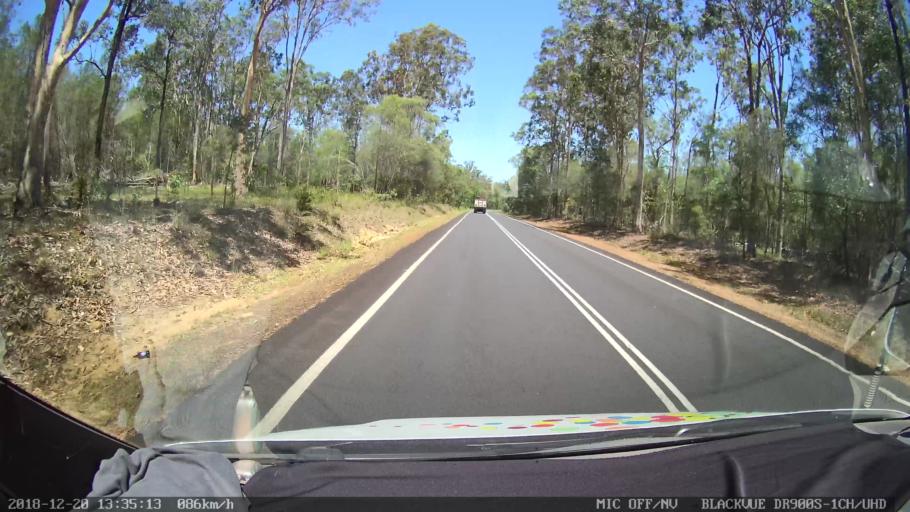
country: AU
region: New South Wales
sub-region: Clarence Valley
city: Gordon
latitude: -29.2671
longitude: 152.9893
